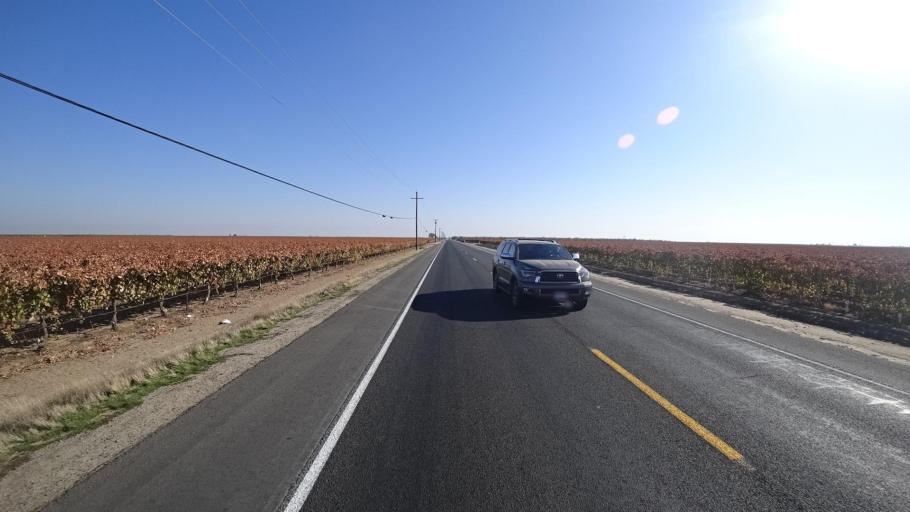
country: US
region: California
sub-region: Kern County
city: Delano
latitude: 35.7178
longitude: -119.2915
